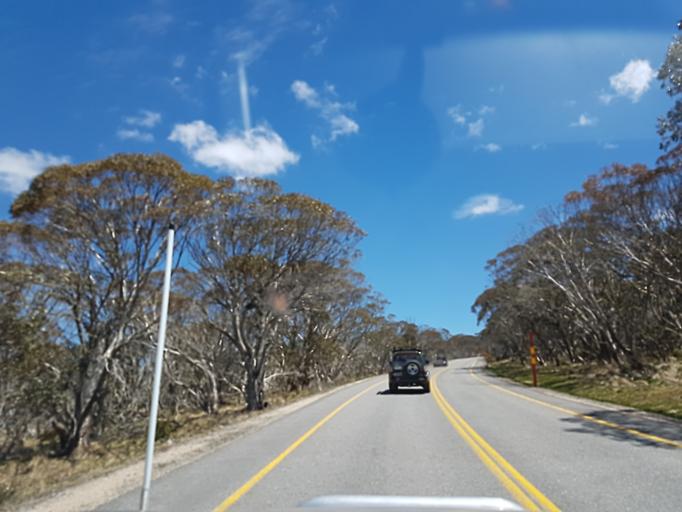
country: AU
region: Victoria
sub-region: Alpine
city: Mount Beauty
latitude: -37.0212
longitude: 147.2319
